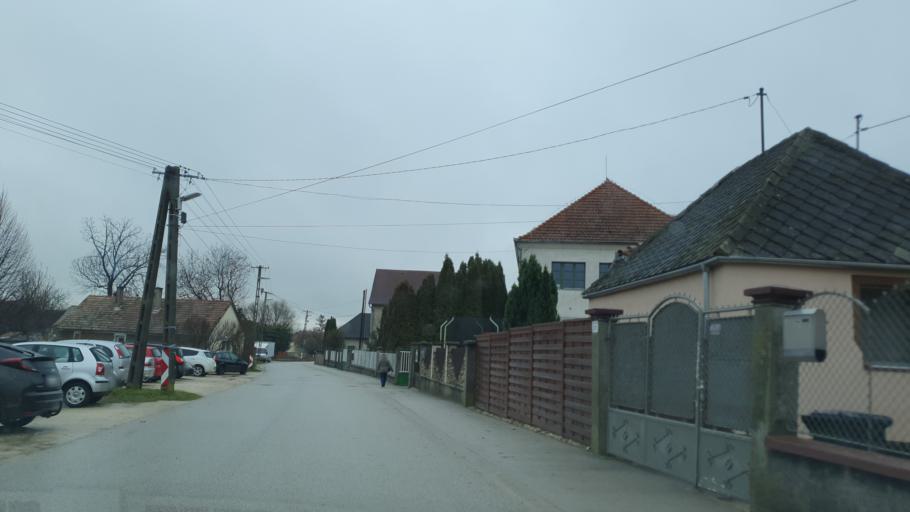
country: HU
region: Veszprem
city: Veszprem
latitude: 47.1436
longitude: 17.9445
